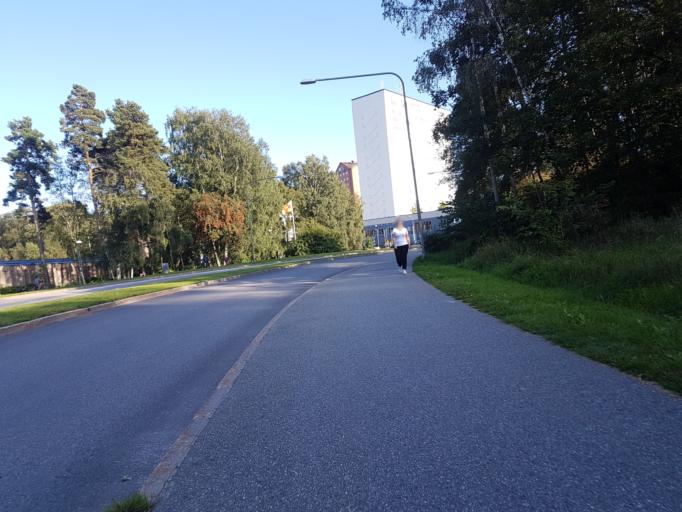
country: SE
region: Stockholm
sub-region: Nacka Kommun
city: Nacka
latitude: 59.2926
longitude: 18.1155
